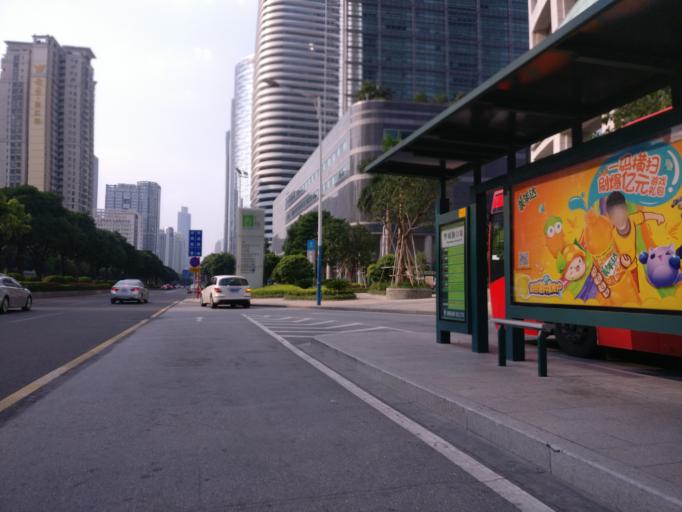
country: CN
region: Guangdong
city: Wushan
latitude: 23.1228
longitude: 113.3160
